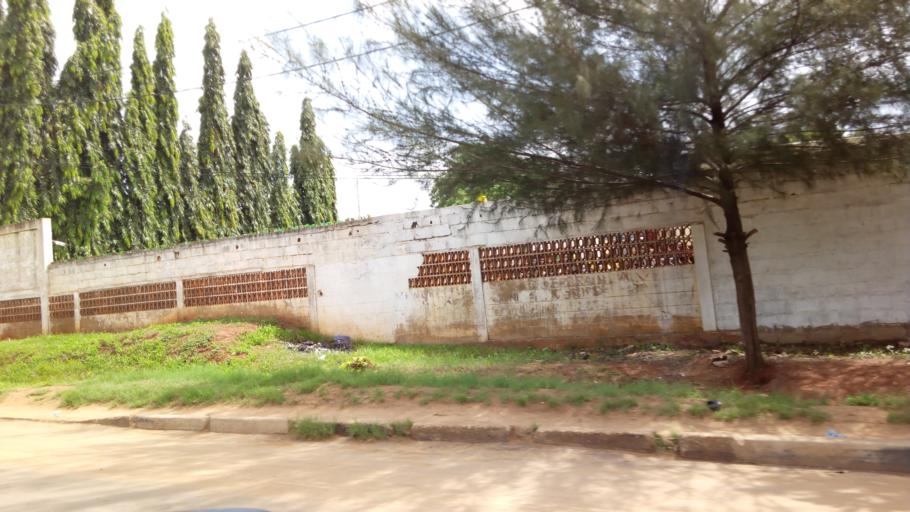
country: TG
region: Maritime
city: Lome
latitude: 6.2346
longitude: 1.2105
